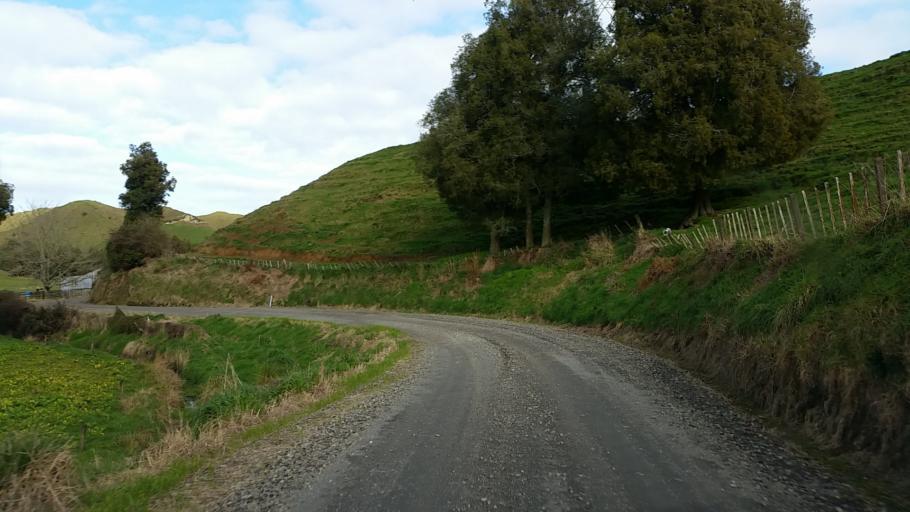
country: NZ
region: Taranaki
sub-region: South Taranaki District
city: Eltham
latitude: -39.2555
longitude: 174.5189
